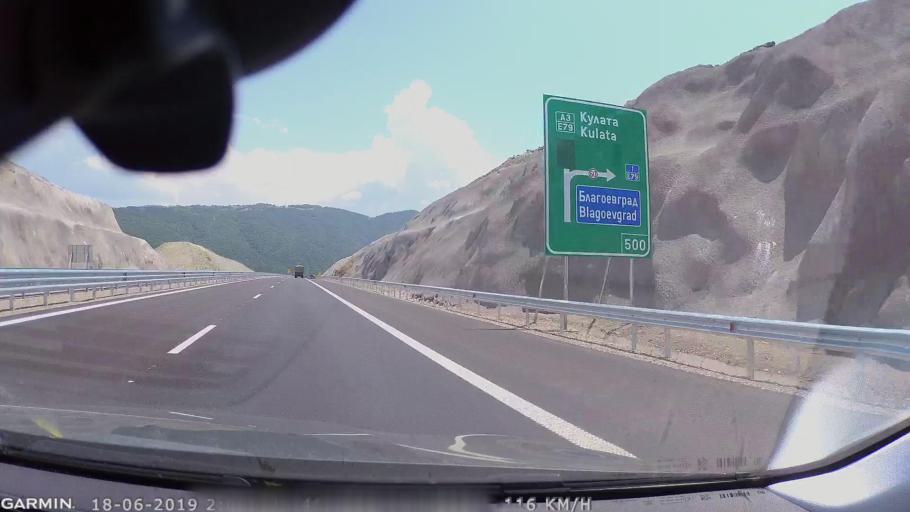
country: BG
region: Blagoevgrad
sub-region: Obshtina Blagoevgrad
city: Blagoevgrad
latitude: 41.9690
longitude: 23.0878
